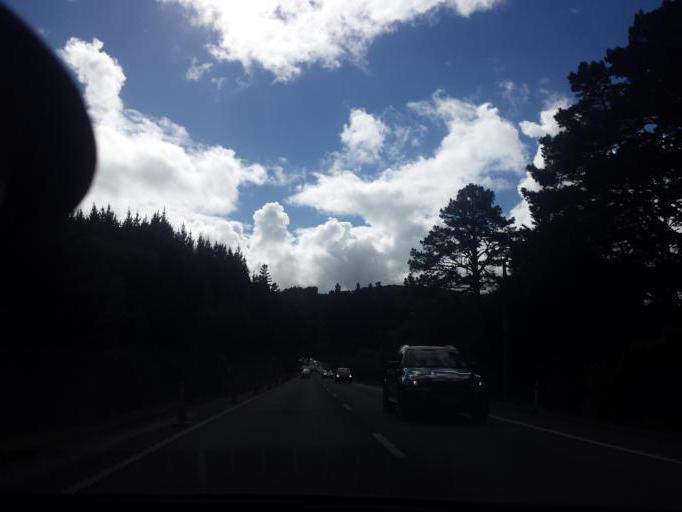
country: NZ
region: Auckland
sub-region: Auckland
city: Warkworth
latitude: -36.5068
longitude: 174.6708
